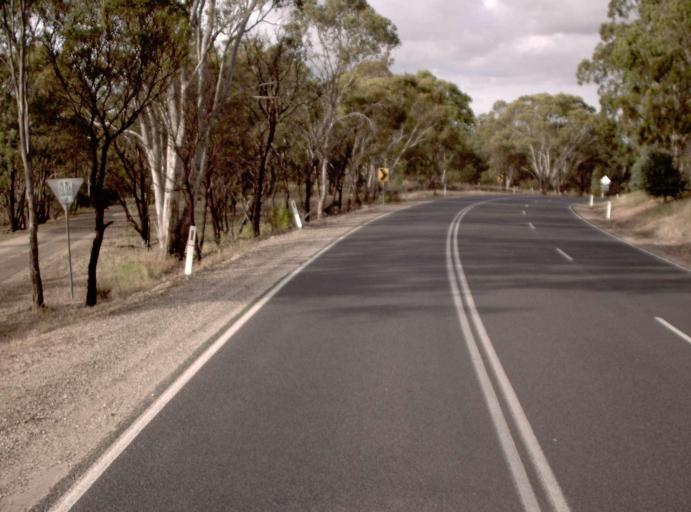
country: AU
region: Victoria
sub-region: Wellington
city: Sale
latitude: -37.9275
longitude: 146.9924
